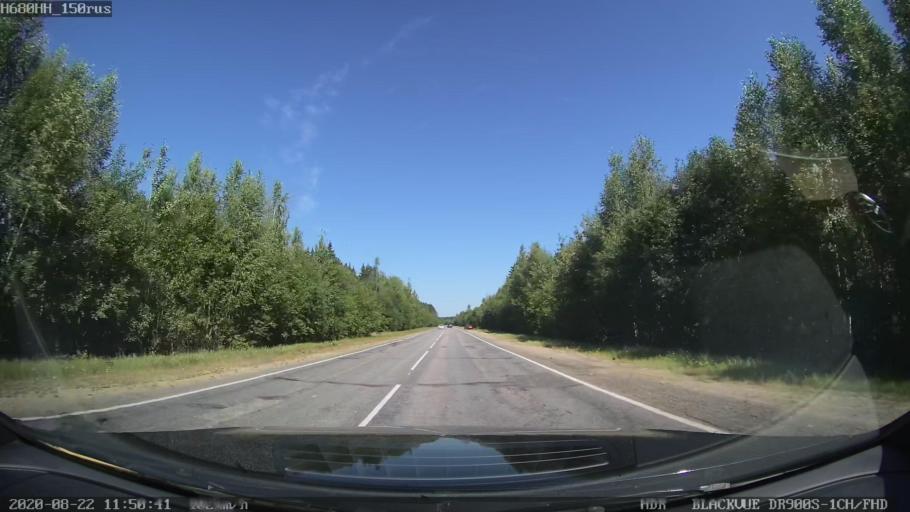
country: RU
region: Tverskaya
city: Sakharovo
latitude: 57.0937
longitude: 36.1174
